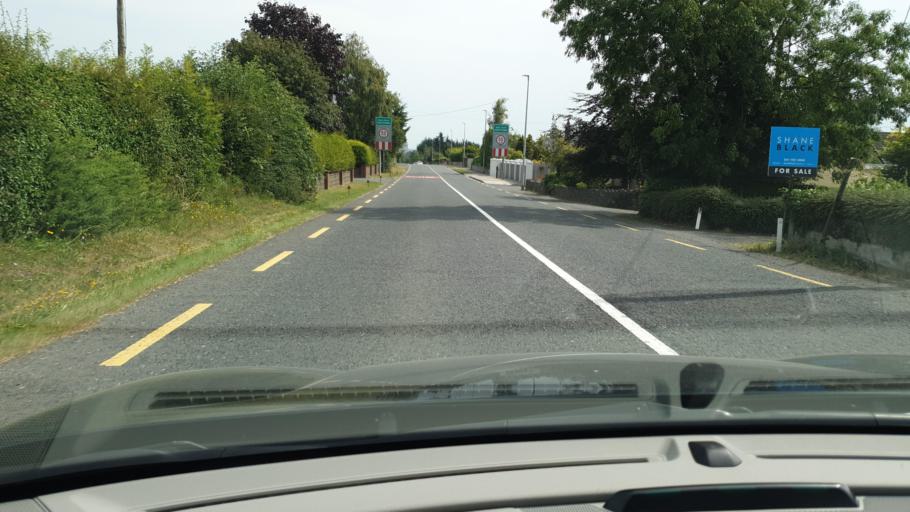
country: IE
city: Kentstown
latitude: 53.6289
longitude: -6.5410
